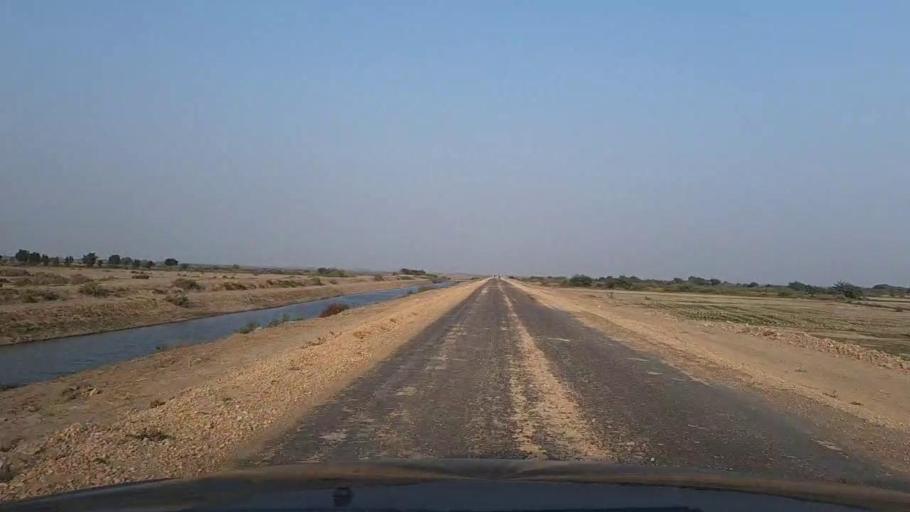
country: PK
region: Sindh
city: Mirpur Sakro
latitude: 24.4222
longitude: 67.7453
